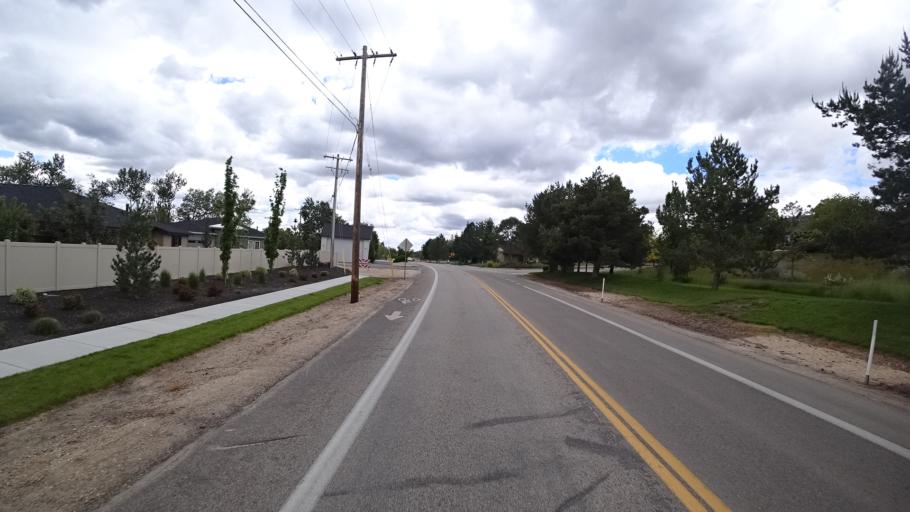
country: US
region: Idaho
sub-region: Ada County
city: Garden City
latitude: 43.6774
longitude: -116.2663
